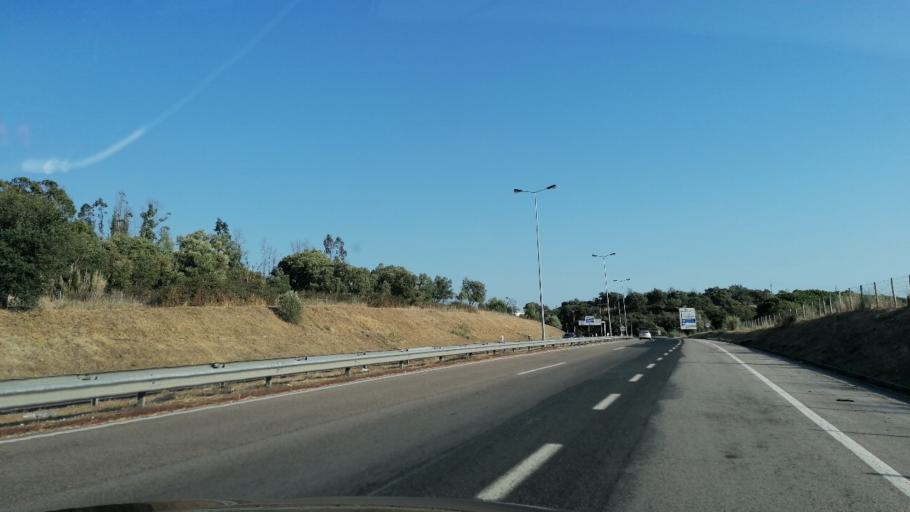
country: PT
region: Santarem
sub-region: Santarem
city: Santarem
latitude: 39.2290
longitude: -8.7046
